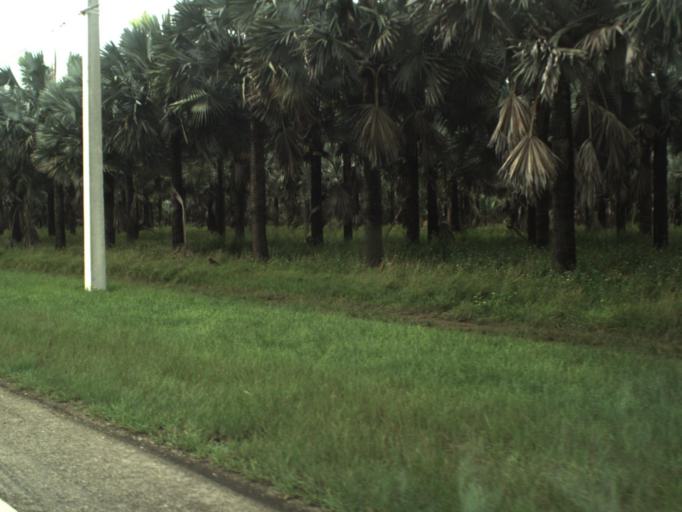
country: US
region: Florida
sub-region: Miami-Dade County
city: Richmond West
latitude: 25.5970
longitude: -80.4786
